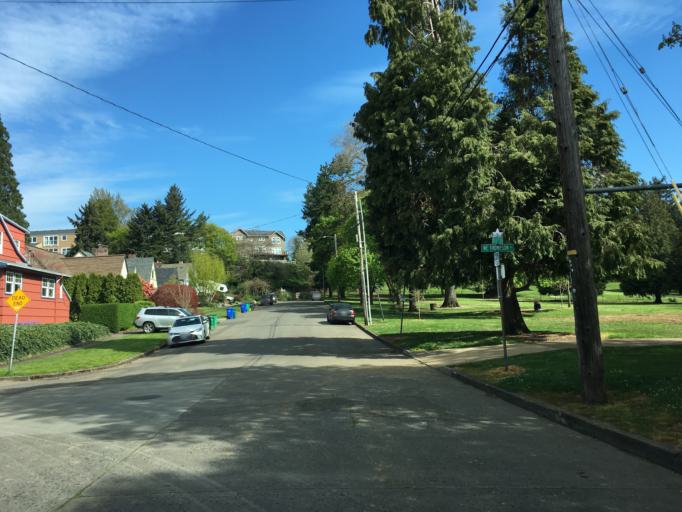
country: US
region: Oregon
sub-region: Multnomah County
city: Lents
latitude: 45.5386
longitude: -122.5995
